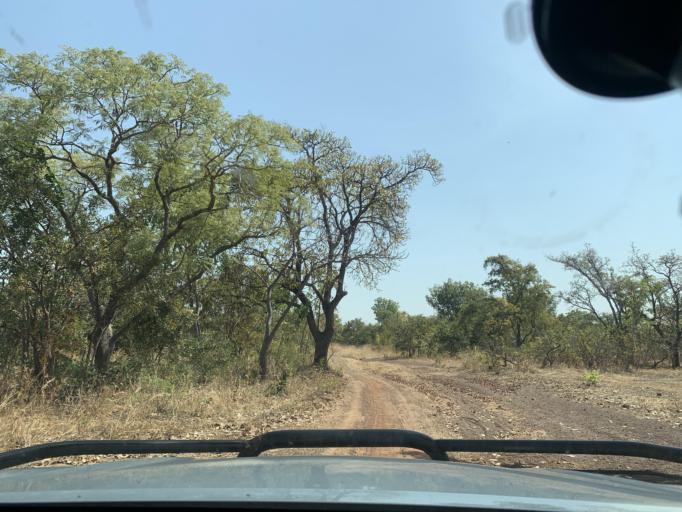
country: ML
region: Sikasso
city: Kolondieba
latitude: 10.8357
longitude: -6.7929
